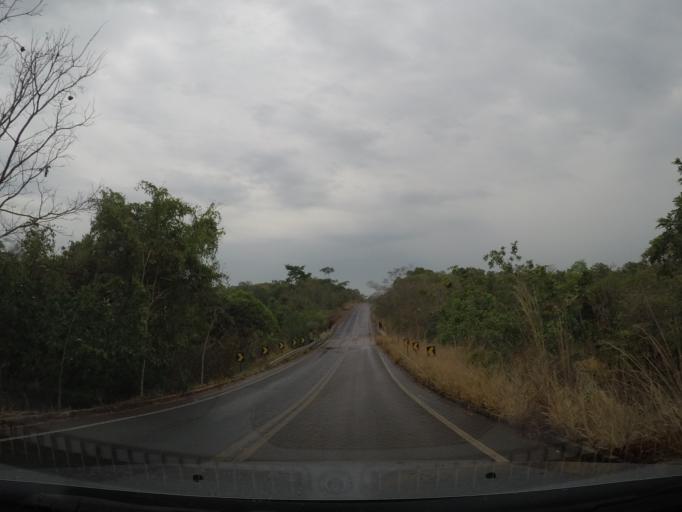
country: BR
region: Goias
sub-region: Pirenopolis
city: Pirenopolis
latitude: -15.8462
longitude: -48.9213
